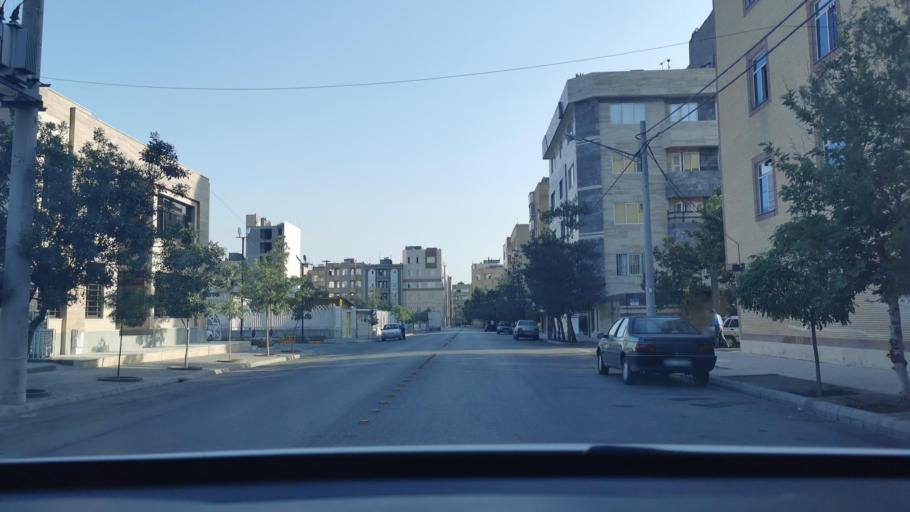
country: IR
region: Razavi Khorasan
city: Mashhad
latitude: 36.3533
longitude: 59.4942
